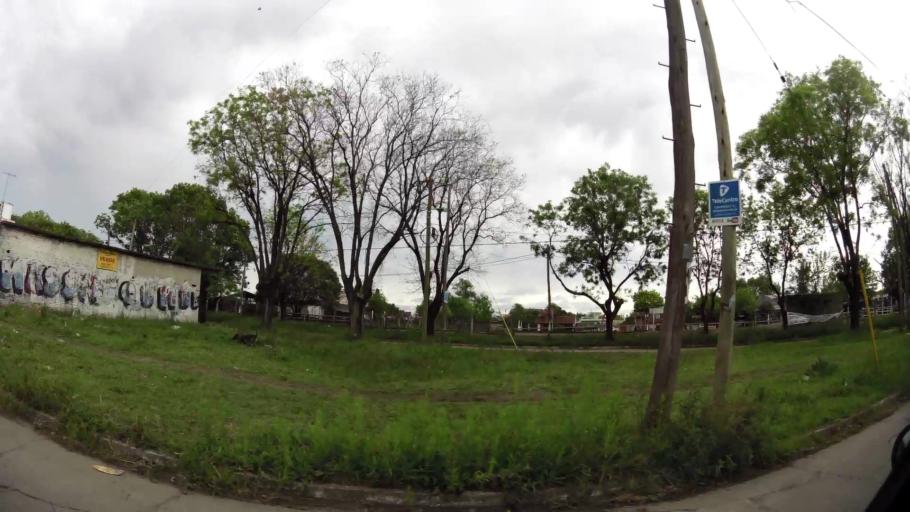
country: AR
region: Buenos Aires
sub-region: Partido de Quilmes
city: Quilmes
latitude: -34.7974
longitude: -58.2758
